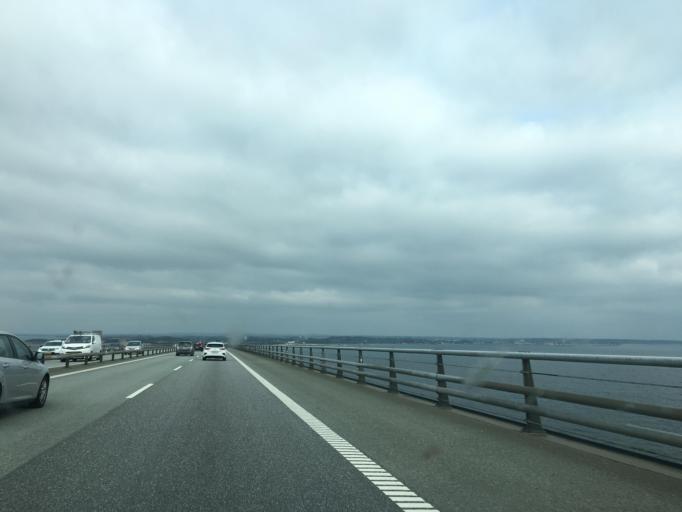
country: DK
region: Zealand
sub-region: Slagelse Kommune
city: Korsor
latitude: 55.3458
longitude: 11.0567
